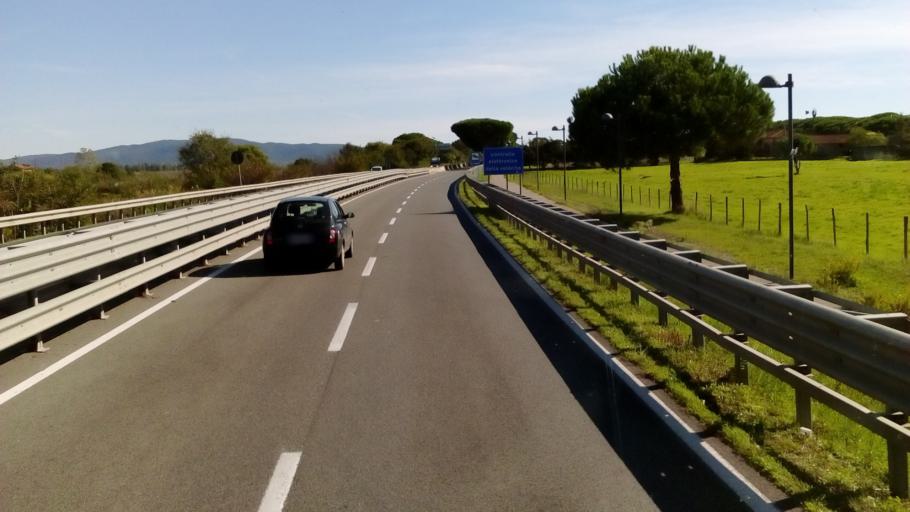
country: IT
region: Tuscany
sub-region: Provincia di Grosseto
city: Fonteblanda
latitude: 42.5446
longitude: 11.1780
